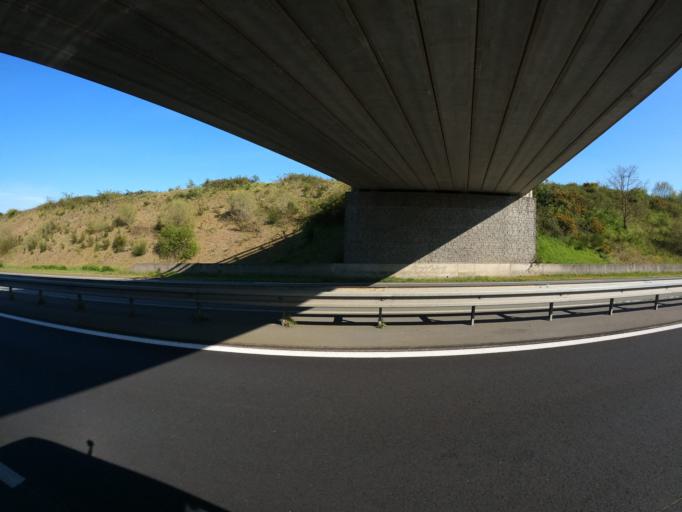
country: FR
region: Pays de la Loire
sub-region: Departement de Maine-et-Loire
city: Saint-Christophe-du-Bois
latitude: 47.0160
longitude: -0.9270
